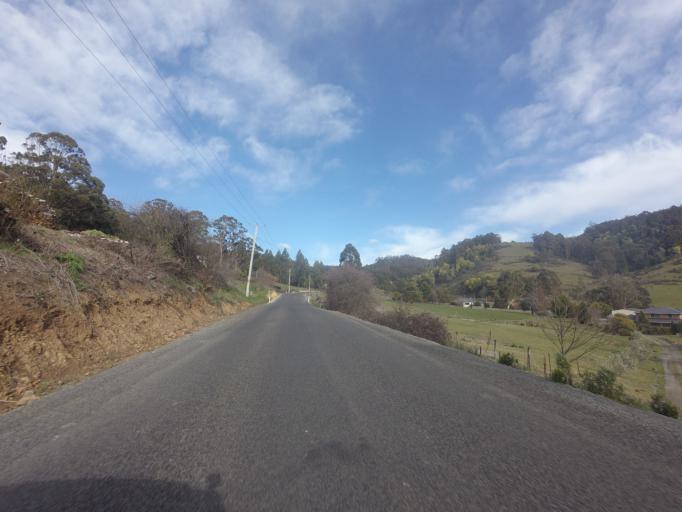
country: AU
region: Tasmania
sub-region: Kingborough
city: Margate
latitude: -42.9927
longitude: 147.1853
